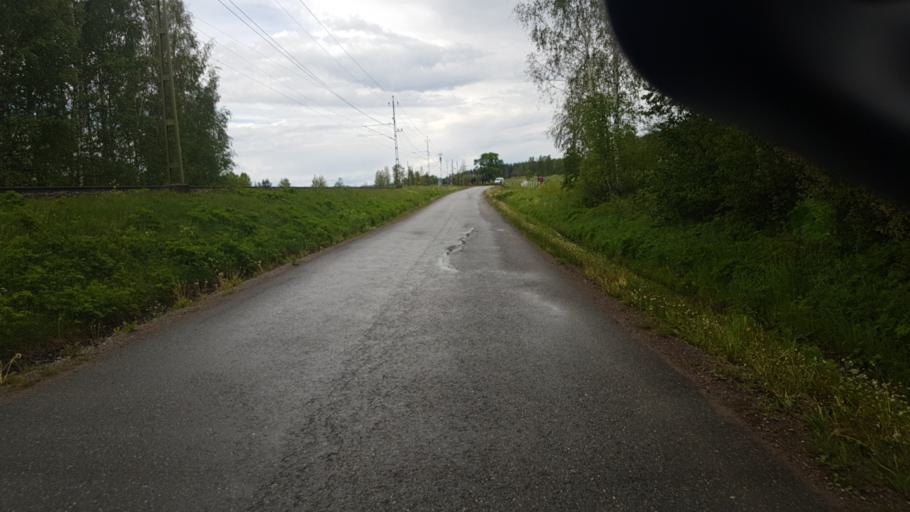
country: SE
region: Vaermland
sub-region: Eda Kommun
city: Amotfors
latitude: 59.7996
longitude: 12.3669
